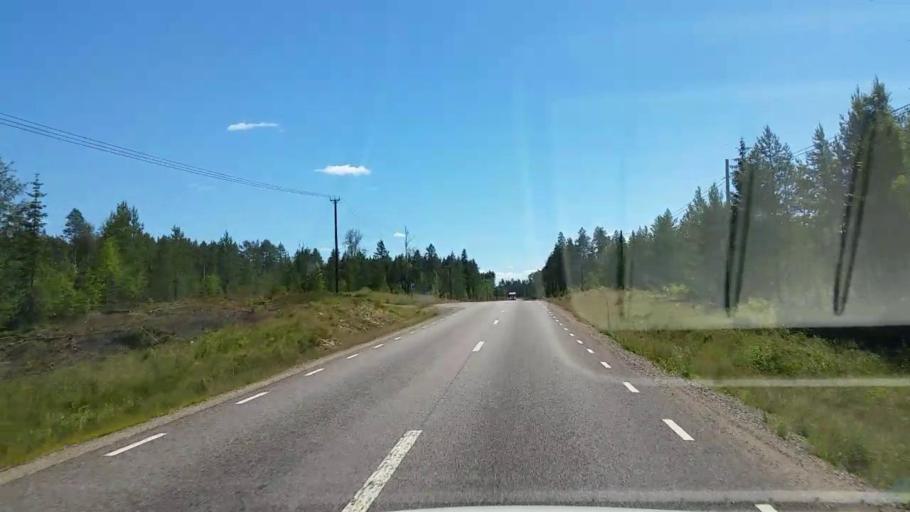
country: SE
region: Gaevleborg
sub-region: Ovanakers Kommun
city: Edsbyn
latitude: 61.4646
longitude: 15.6981
